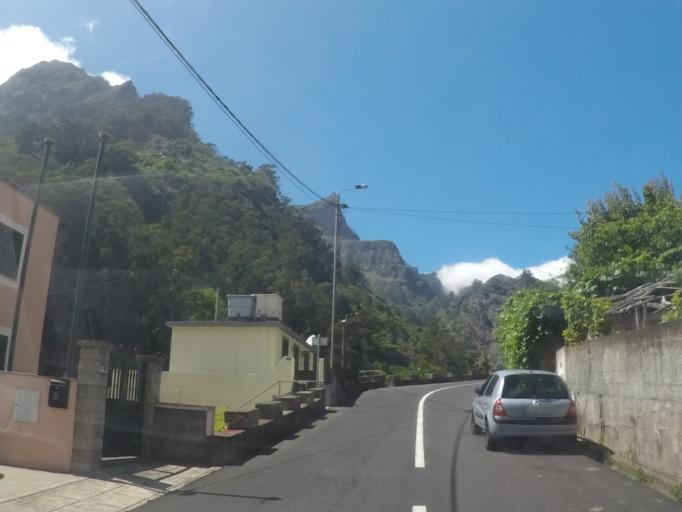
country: PT
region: Madeira
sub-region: Camara de Lobos
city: Curral das Freiras
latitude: 32.7158
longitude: -16.9688
